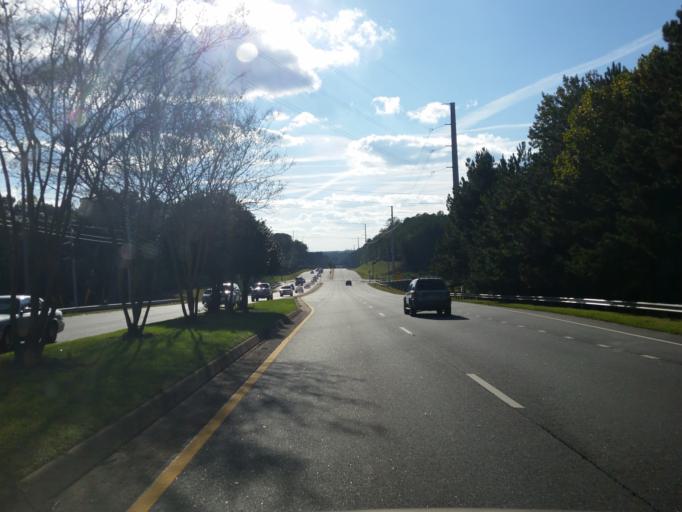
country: US
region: Georgia
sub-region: Paulding County
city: Hiram
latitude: 33.9391
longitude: -84.7087
